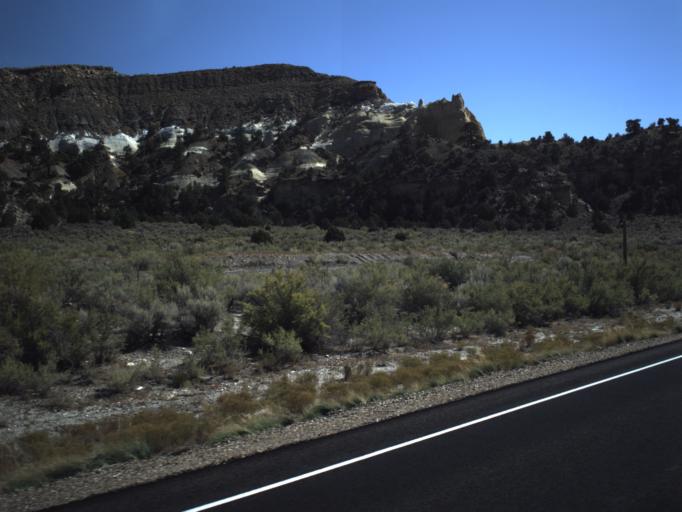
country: US
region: Utah
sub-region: Garfield County
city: Panguitch
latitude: 37.5836
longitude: -111.9843
